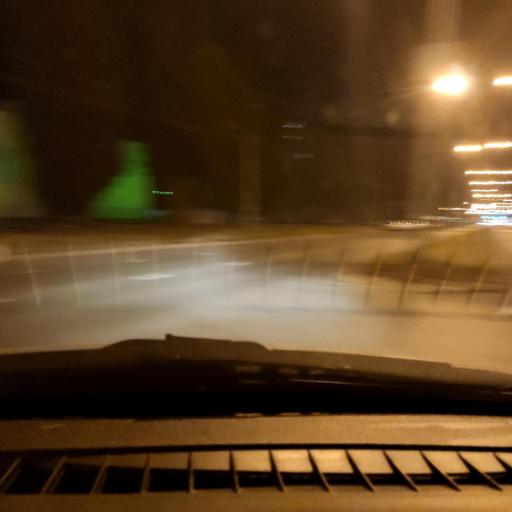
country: RU
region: Samara
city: Tol'yatti
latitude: 53.5380
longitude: 49.3148
